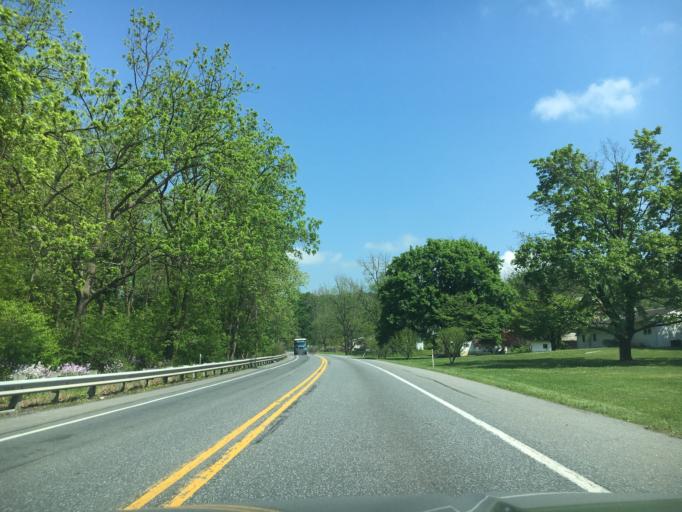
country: US
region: Pennsylvania
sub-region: Berks County
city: New Berlinville
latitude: 40.3523
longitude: -75.6626
